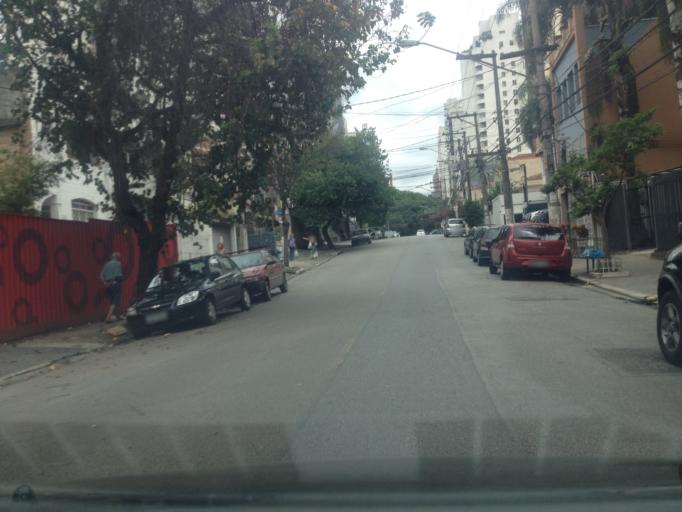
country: BR
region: Sao Paulo
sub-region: Sao Paulo
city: Sao Paulo
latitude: -23.5614
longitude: -46.6770
